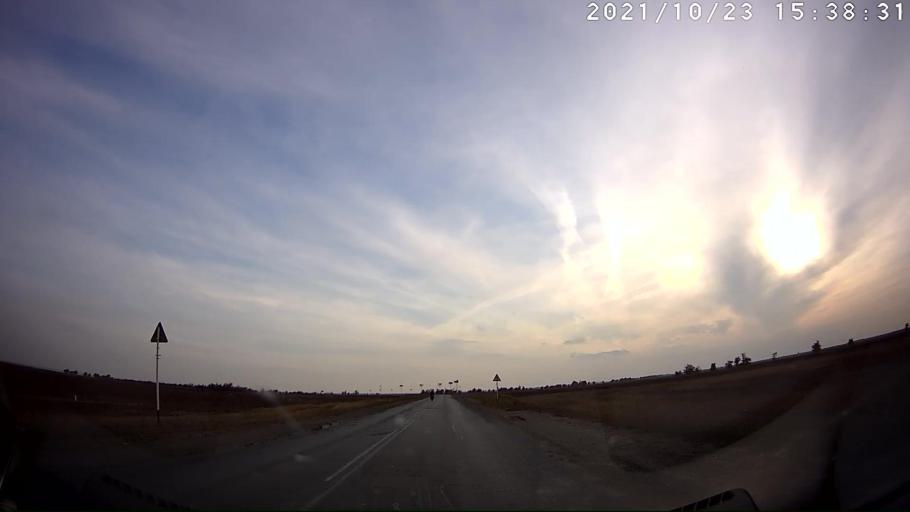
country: RU
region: Volgograd
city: Bereslavka
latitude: 48.1333
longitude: 44.1199
